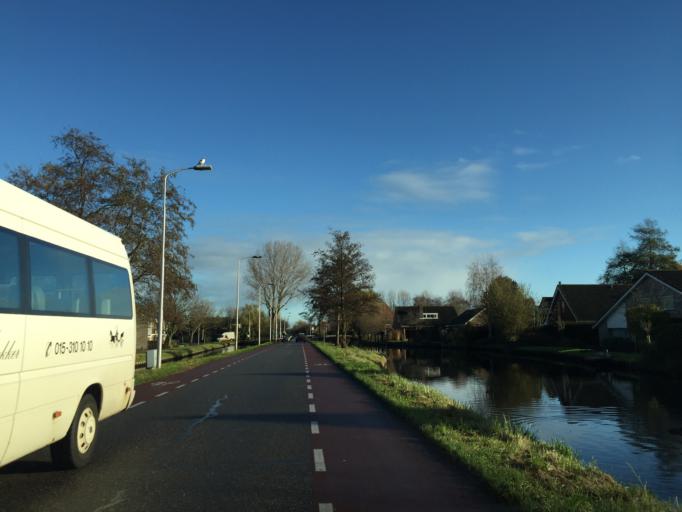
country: NL
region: South Holland
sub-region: Gemeente Den Haag
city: Ypenburg
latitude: 52.0451
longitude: 4.3993
